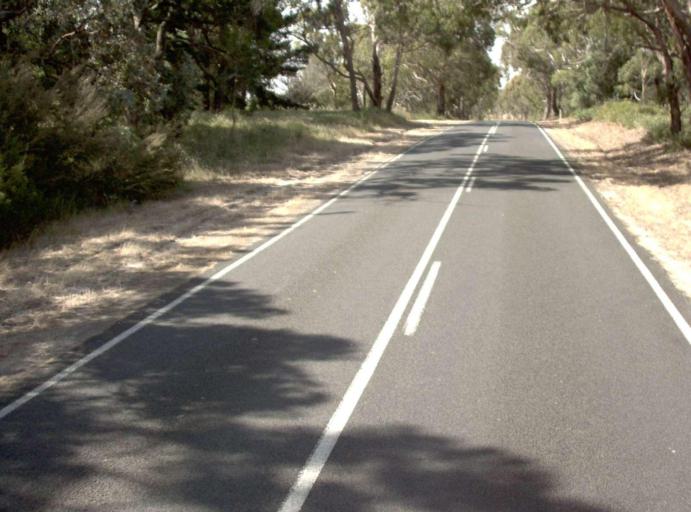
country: AU
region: Victoria
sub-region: Wellington
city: Sale
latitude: -38.2950
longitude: 147.1546
